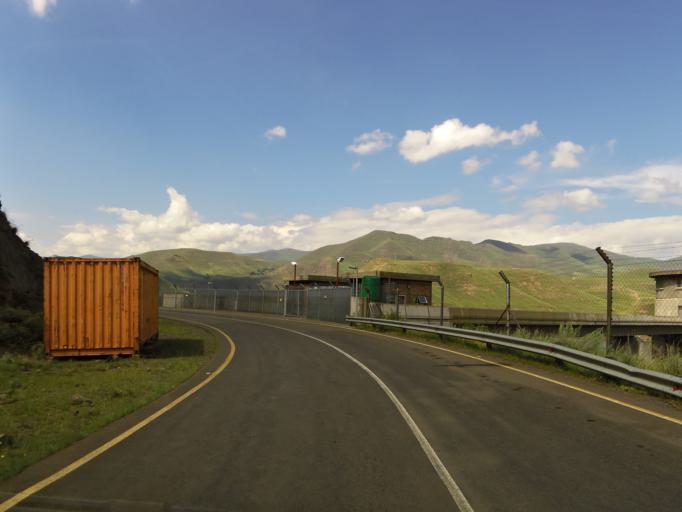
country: LS
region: Thaba-Tseka
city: Thaba-Tseka
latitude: -29.1722
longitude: 28.4815
